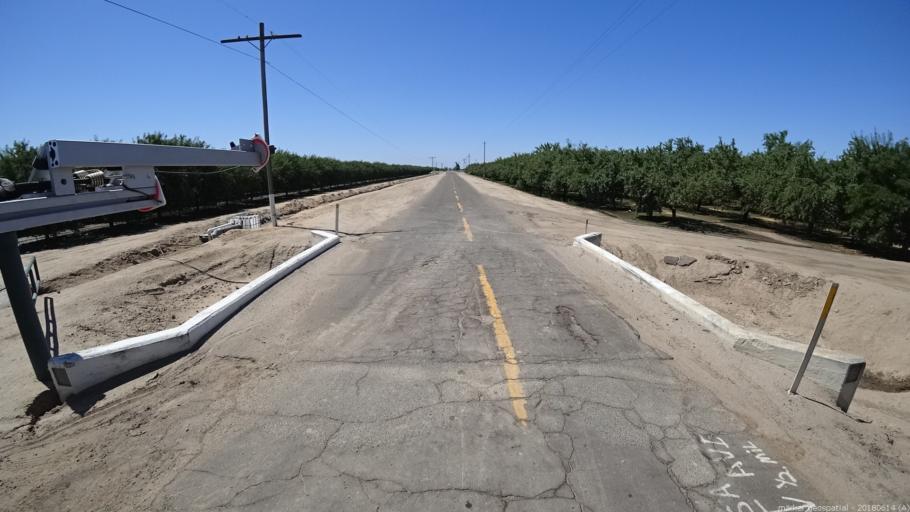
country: US
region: California
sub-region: Madera County
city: Fairmead
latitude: 36.9855
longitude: -120.1844
